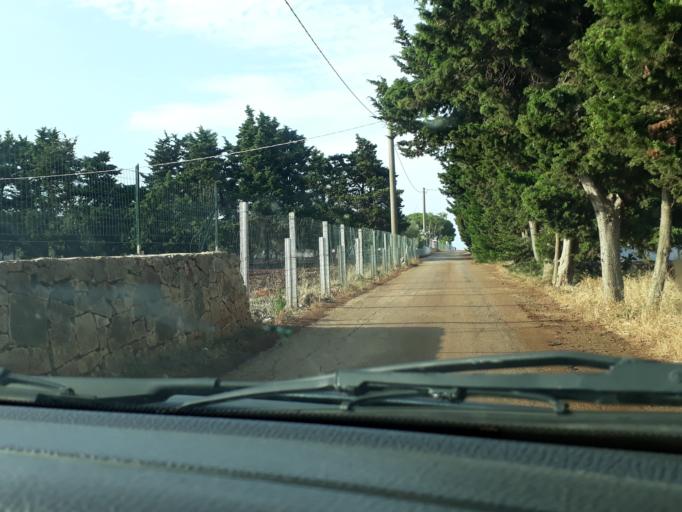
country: IT
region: Apulia
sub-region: Provincia di Brindisi
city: Carovigno
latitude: 40.7591
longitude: 17.6831
